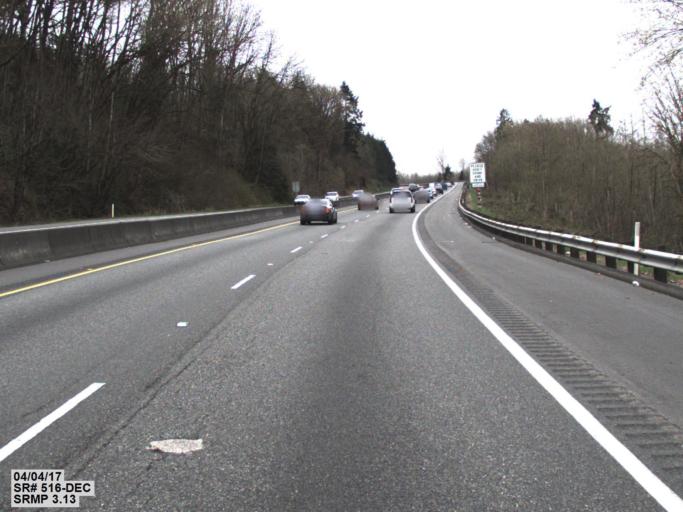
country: US
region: Washington
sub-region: King County
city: Kent
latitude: 47.3829
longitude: -122.2768
